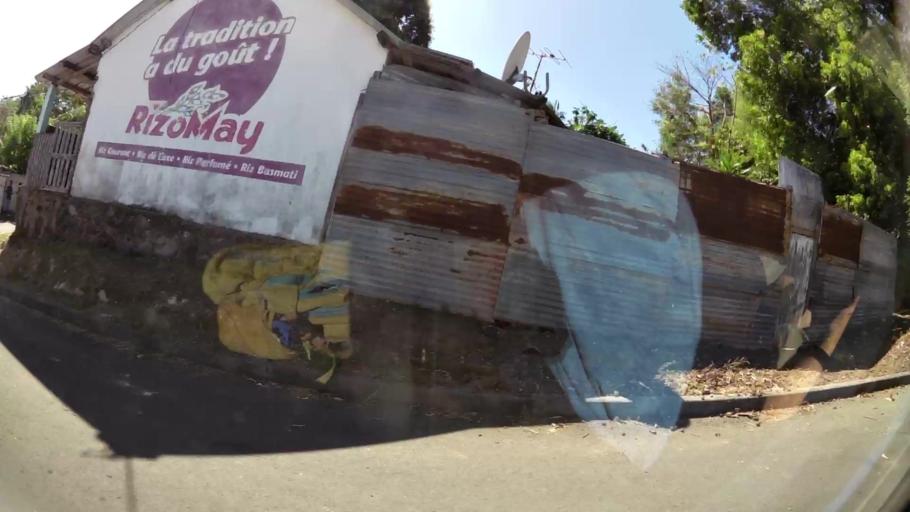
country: YT
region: Pamandzi
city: Pamandzi
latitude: -12.7977
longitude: 45.2783
